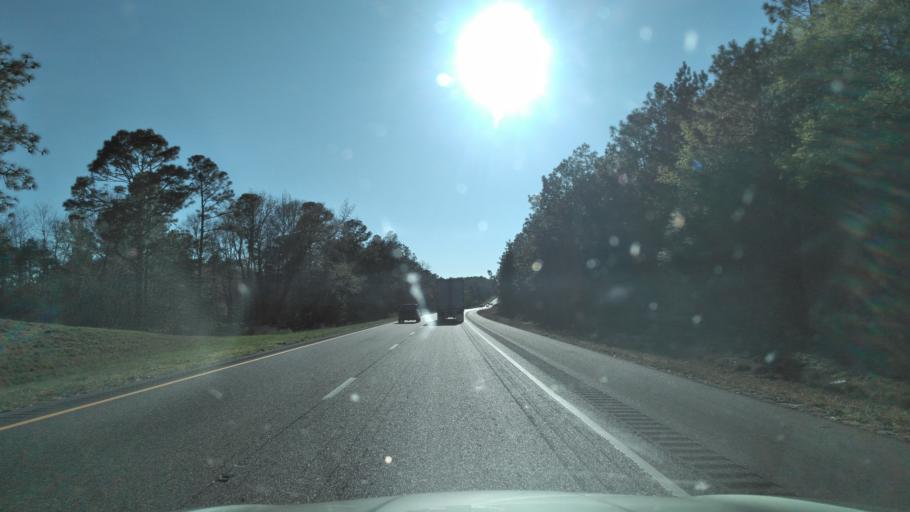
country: US
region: Alabama
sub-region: Escambia County
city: Atmore
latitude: 31.0664
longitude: -87.5613
